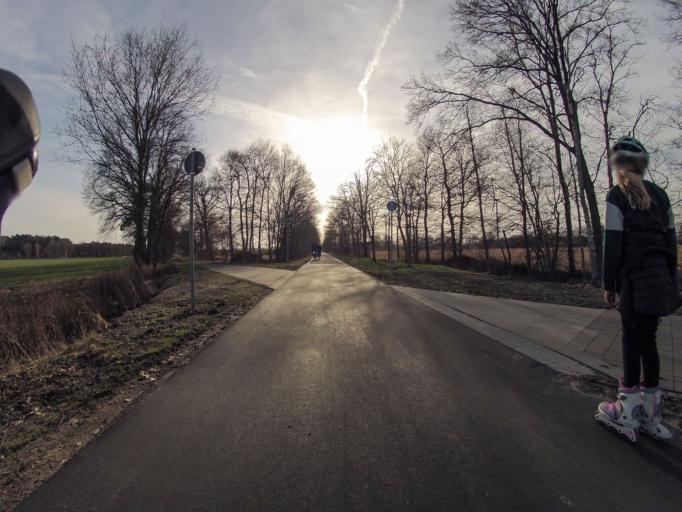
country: DE
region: North Rhine-Westphalia
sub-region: Regierungsbezirk Munster
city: Neuenkirchen
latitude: 52.2272
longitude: 7.4283
